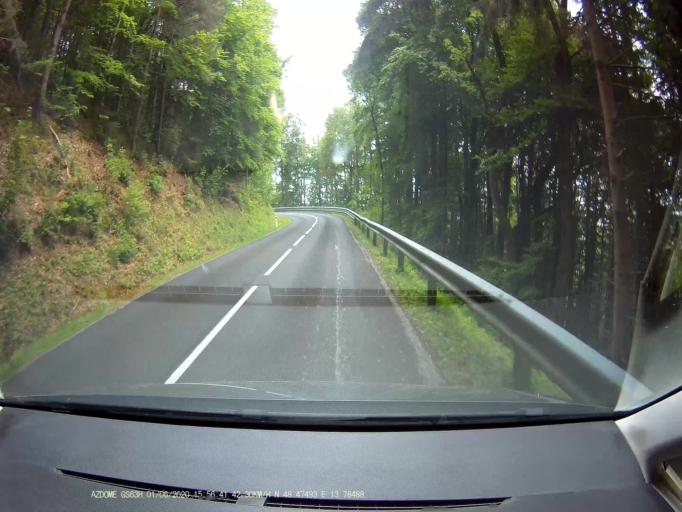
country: AT
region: Upper Austria
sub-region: Politischer Bezirk Rohrbach
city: Pfarrkirchen im Muehlkreis
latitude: 48.4747
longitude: 13.7850
